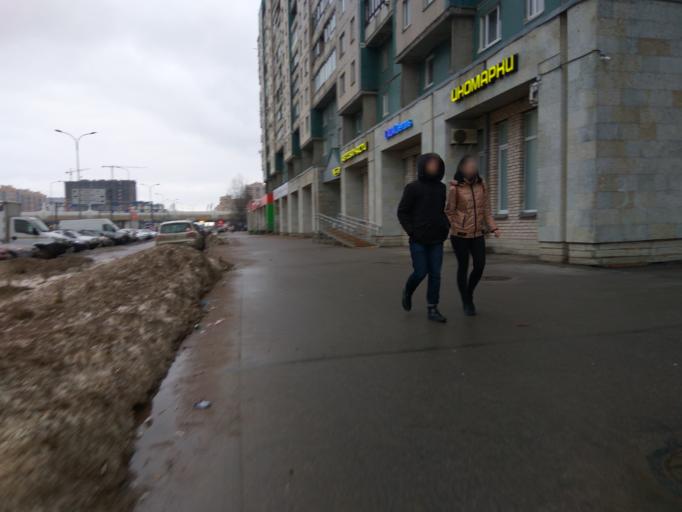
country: RU
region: St.-Petersburg
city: Staraya Derevnya
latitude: 60.0036
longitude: 30.2393
